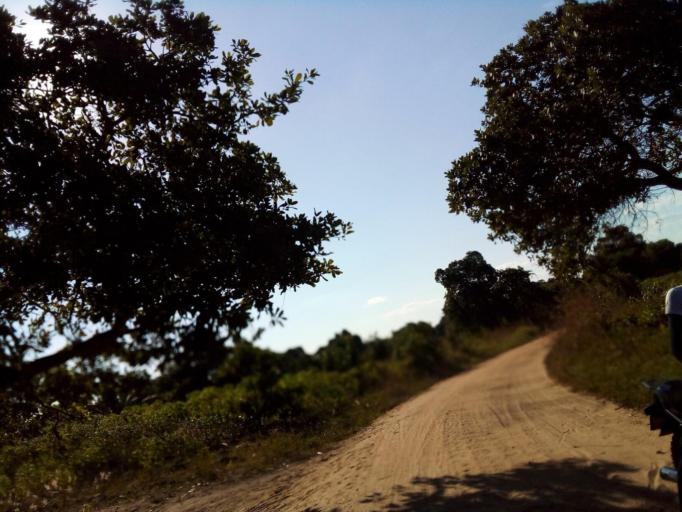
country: MZ
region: Zambezia
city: Quelimane
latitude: -17.5272
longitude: 36.6167
